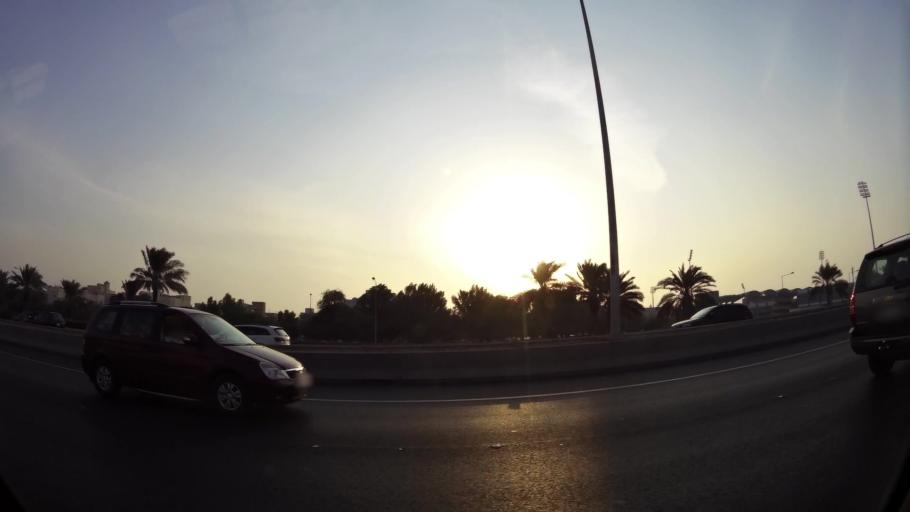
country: KW
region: Muhafazat Hawalli
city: Salwa
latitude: 29.2907
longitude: 48.0716
